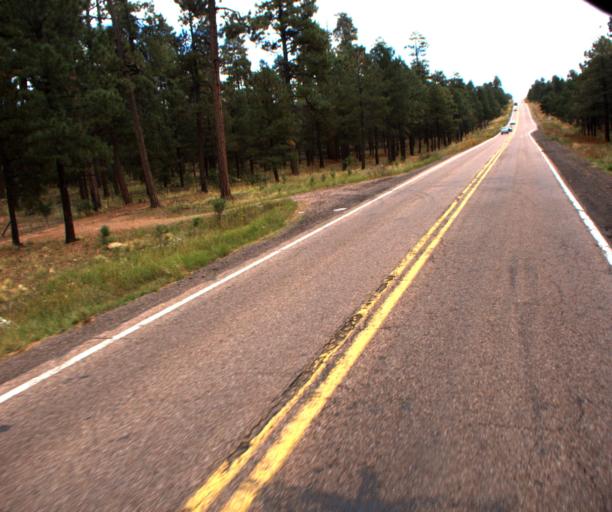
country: US
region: Arizona
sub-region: Navajo County
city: Heber-Overgaard
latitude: 34.3309
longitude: -110.7672
